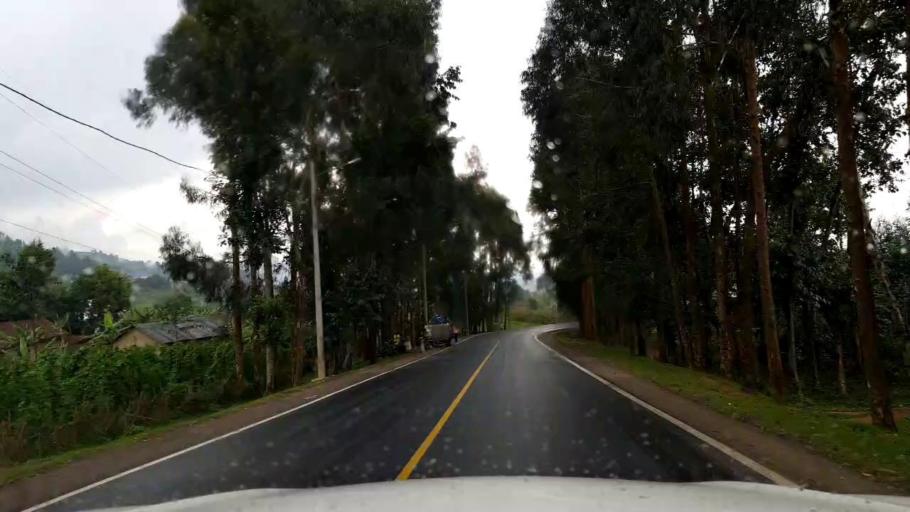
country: RW
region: Western Province
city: Gisenyi
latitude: -1.6715
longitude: 29.3619
